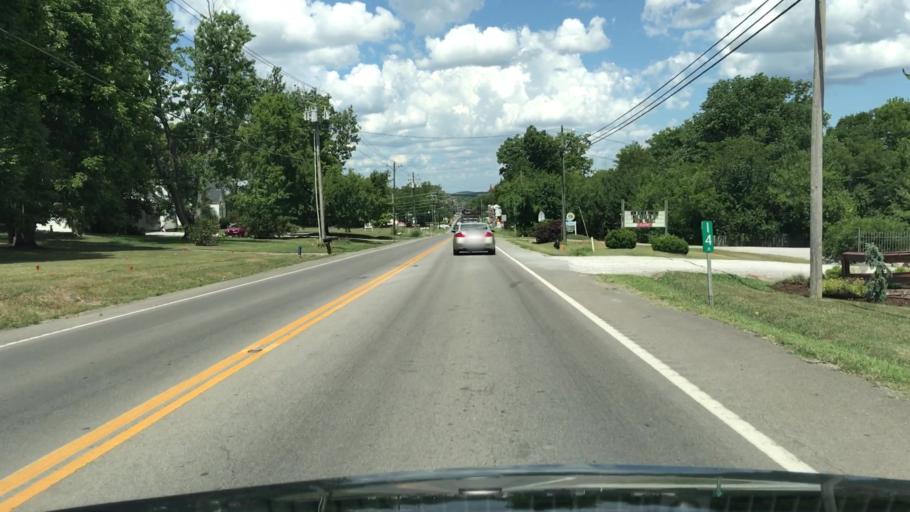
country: US
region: Tennessee
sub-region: Williamson County
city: Nolensville
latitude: 35.9470
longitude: -86.6662
